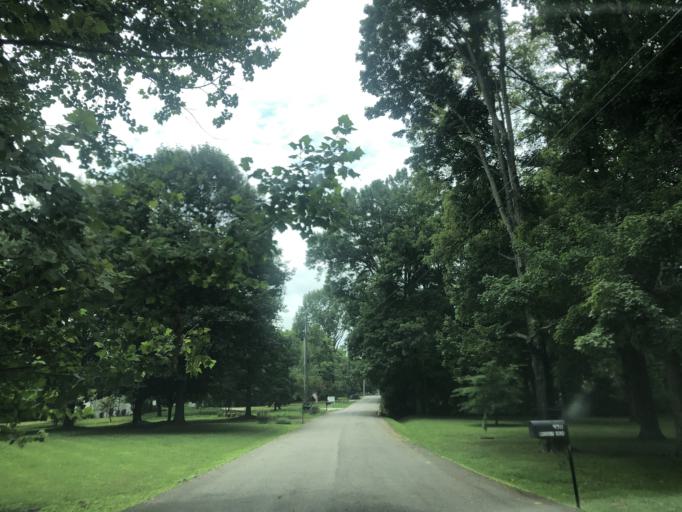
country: US
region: Tennessee
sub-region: Davidson County
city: Oak Hill
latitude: 36.0855
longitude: -86.7961
